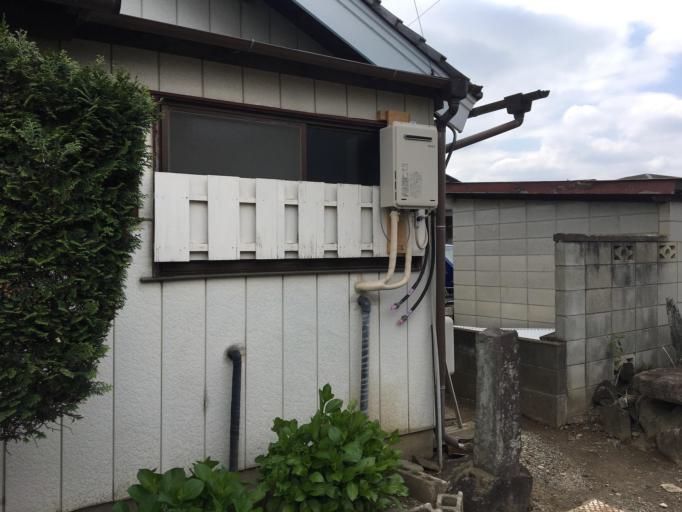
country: JP
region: Gunma
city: Isesaki
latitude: 36.2917
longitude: 139.1673
